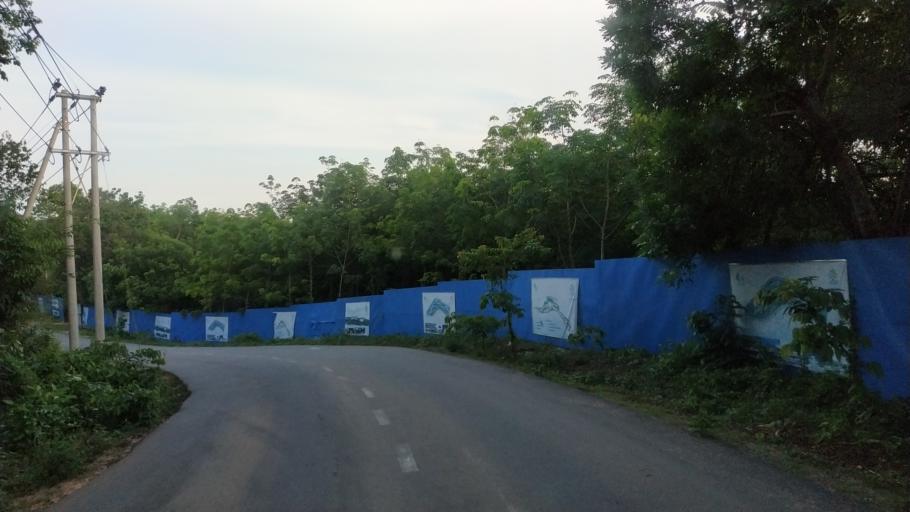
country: MM
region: Mon
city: Kyaikto
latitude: 17.4167
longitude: 97.0707
